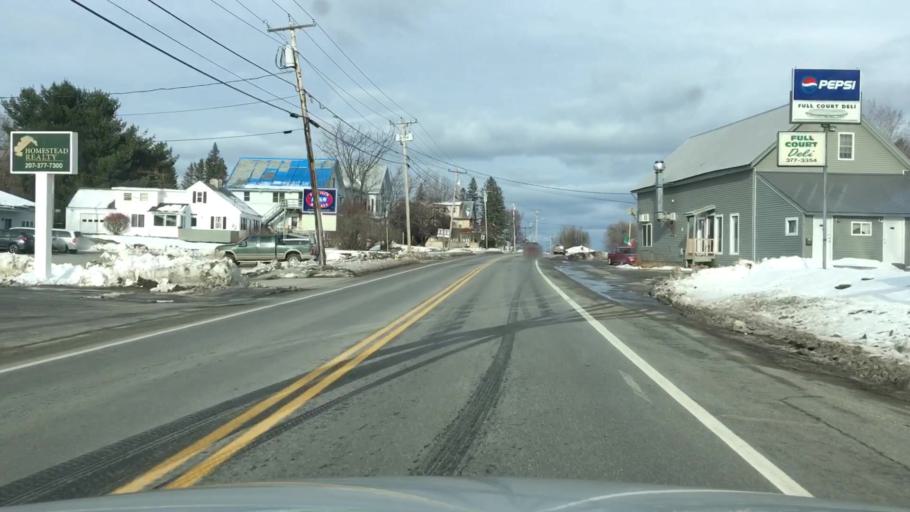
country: US
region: Maine
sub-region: Kennebec County
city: Winthrop
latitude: 44.3032
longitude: -69.9783
